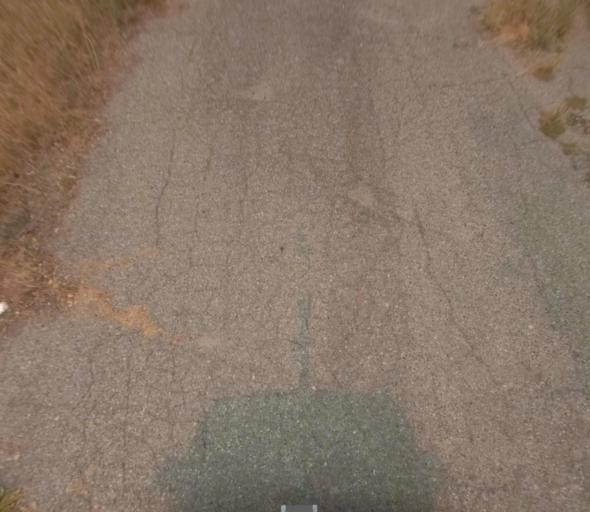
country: US
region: California
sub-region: Madera County
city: Oakhurst
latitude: 37.3334
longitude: -119.6398
